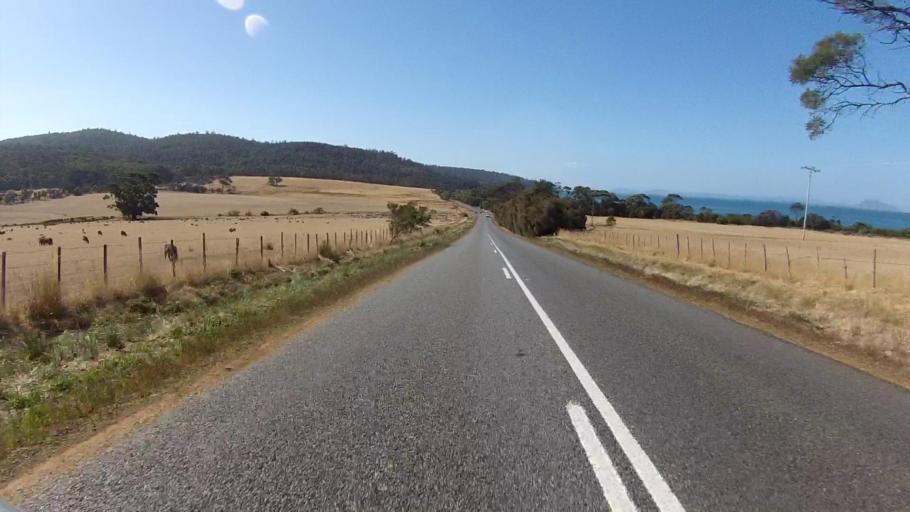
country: AU
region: Tasmania
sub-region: Sorell
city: Sorell
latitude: -42.2499
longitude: 148.0081
